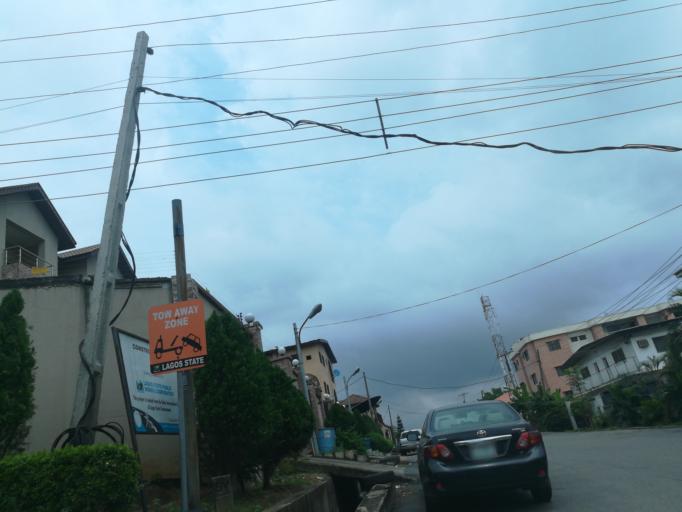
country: NG
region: Lagos
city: Ojota
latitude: 6.5881
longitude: 3.3661
